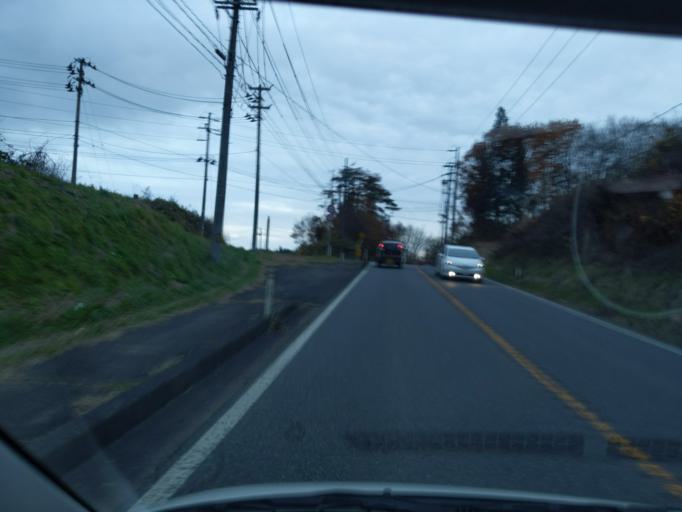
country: JP
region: Iwate
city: Ichinoseki
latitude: 39.0112
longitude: 141.3281
